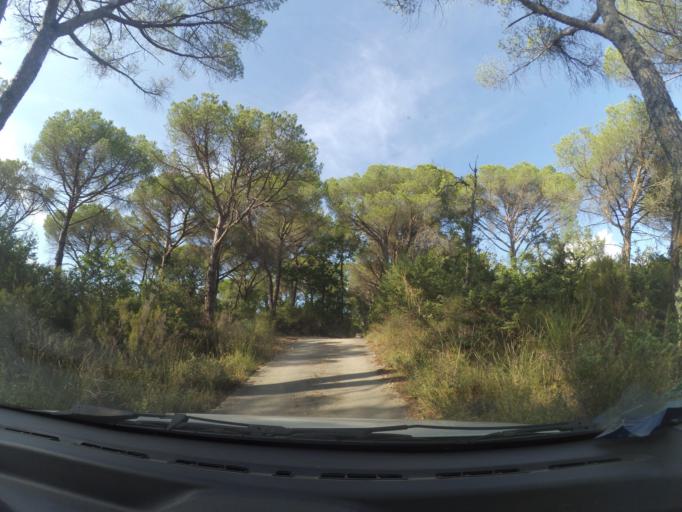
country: IT
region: Tuscany
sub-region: Province of Arezzo
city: Castiglion Fibocchi
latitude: 43.5310
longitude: 11.7822
